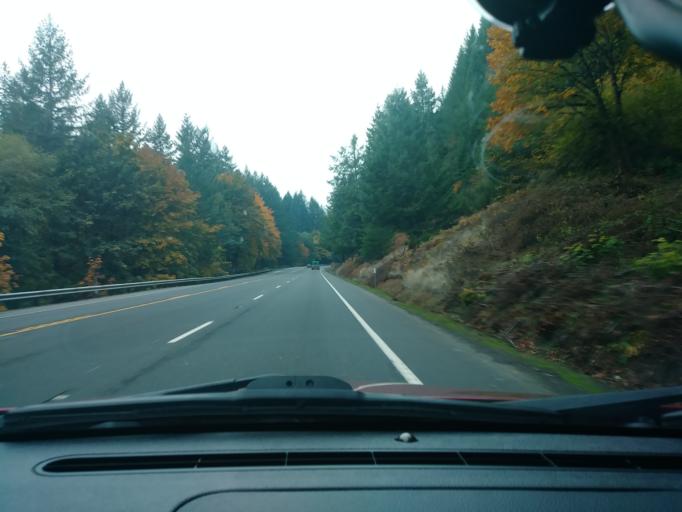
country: US
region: Oregon
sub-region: Washington County
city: Banks
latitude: 45.6159
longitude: -123.1945
